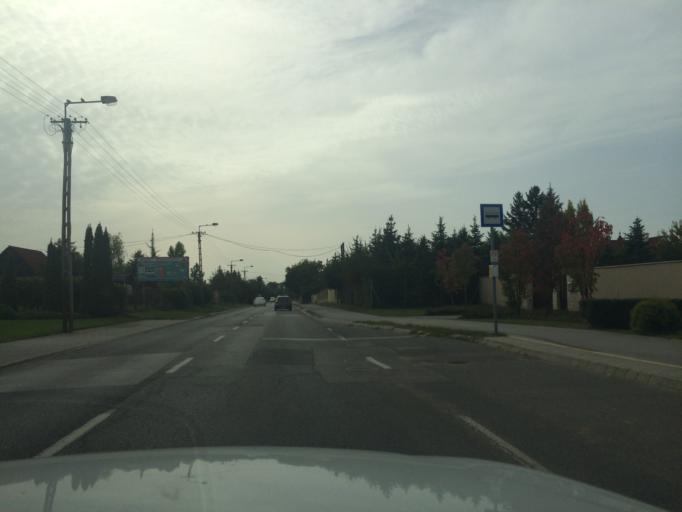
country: HU
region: Szabolcs-Szatmar-Bereg
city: Nyiregyhaza
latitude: 47.9894
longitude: 21.7296
